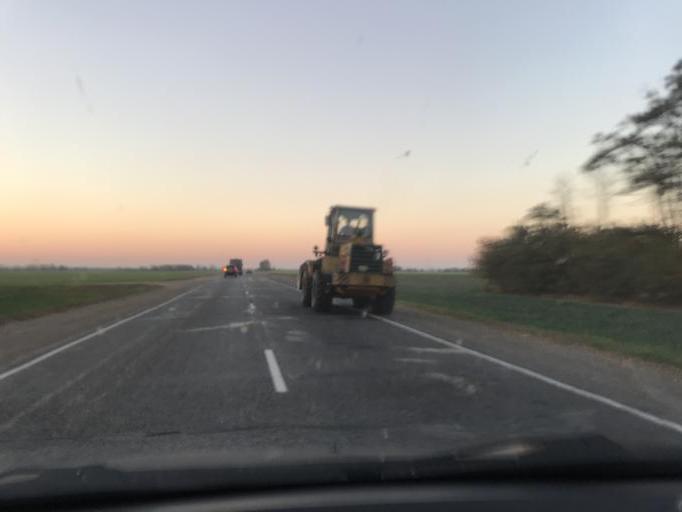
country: BY
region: Gomel
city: Horad Rechytsa
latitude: 52.2088
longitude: 30.5325
